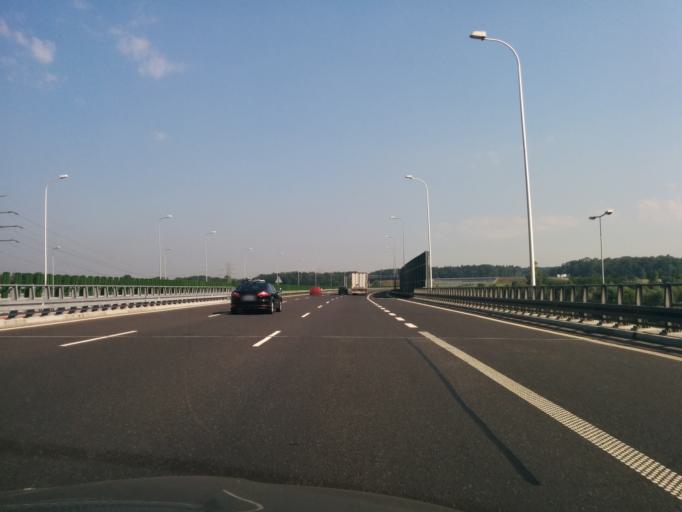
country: PL
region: Silesian Voivodeship
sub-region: Gliwice
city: Gliwice
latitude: 50.3108
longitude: 18.7266
